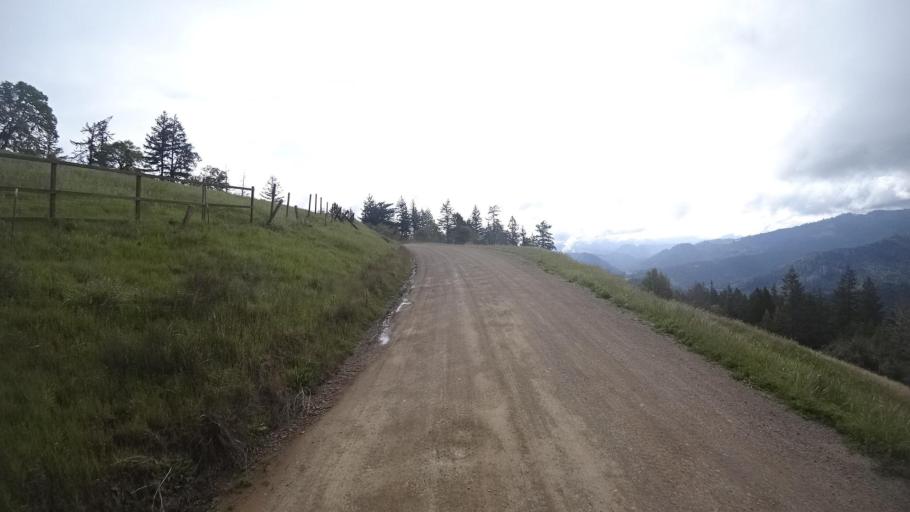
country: US
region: California
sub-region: Humboldt County
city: Redway
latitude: 40.2535
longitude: -123.7655
